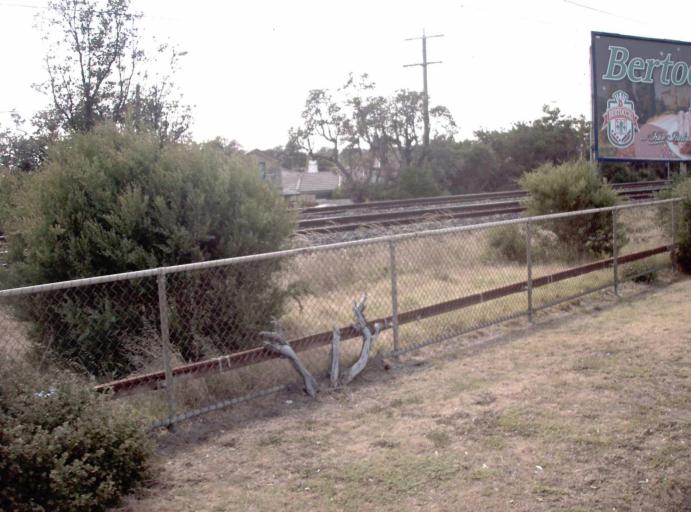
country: AU
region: Victoria
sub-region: Kingston
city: Aspendale
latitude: -38.0233
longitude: 145.0995
